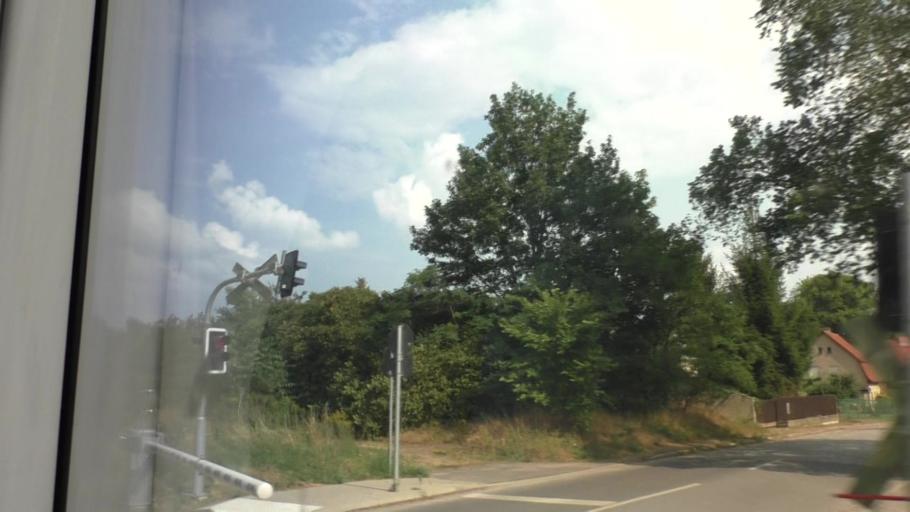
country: DE
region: Brandenburg
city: Konigs Wusterhausen
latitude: 52.3007
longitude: 13.6969
